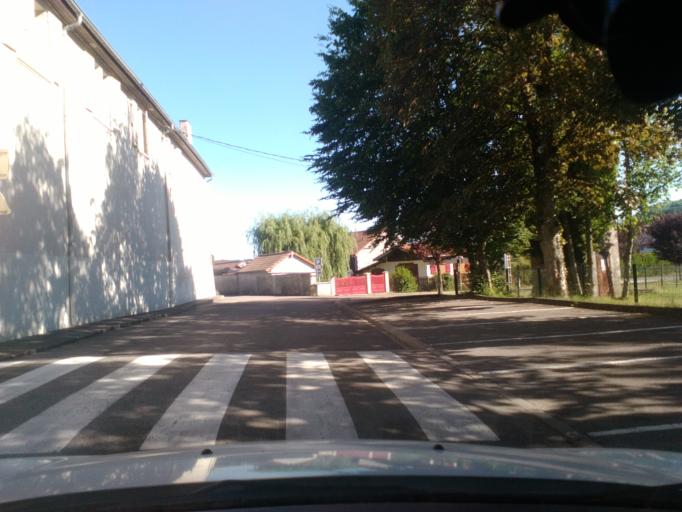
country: FR
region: Lorraine
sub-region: Departement des Vosges
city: Mirecourt
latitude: 48.2806
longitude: 6.1318
